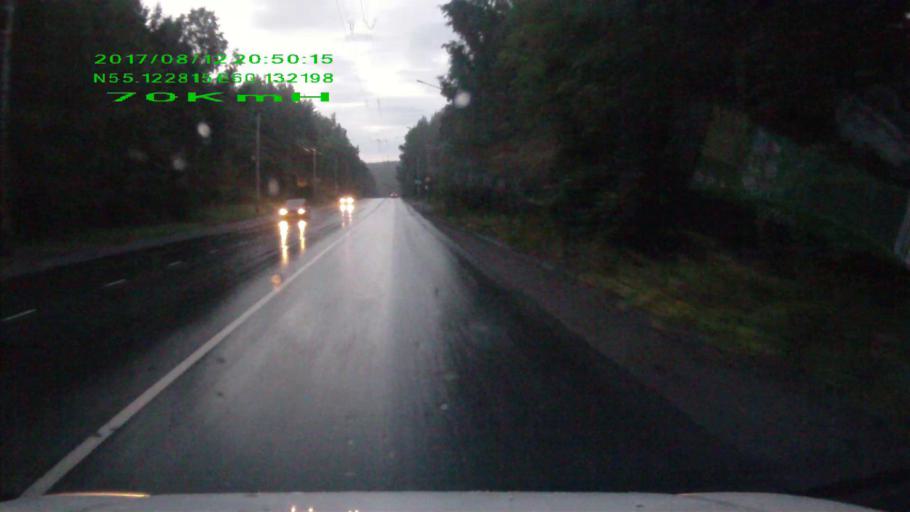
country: RU
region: Chelyabinsk
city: Turgoyak
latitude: 55.1229
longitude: 60.1322
